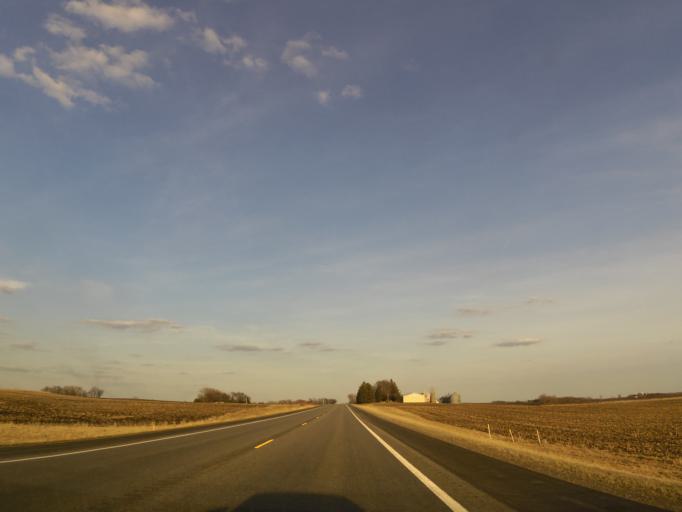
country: US
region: Minnesota
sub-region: McLeod County
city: Glencoe
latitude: 44.7396
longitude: -94.2466
